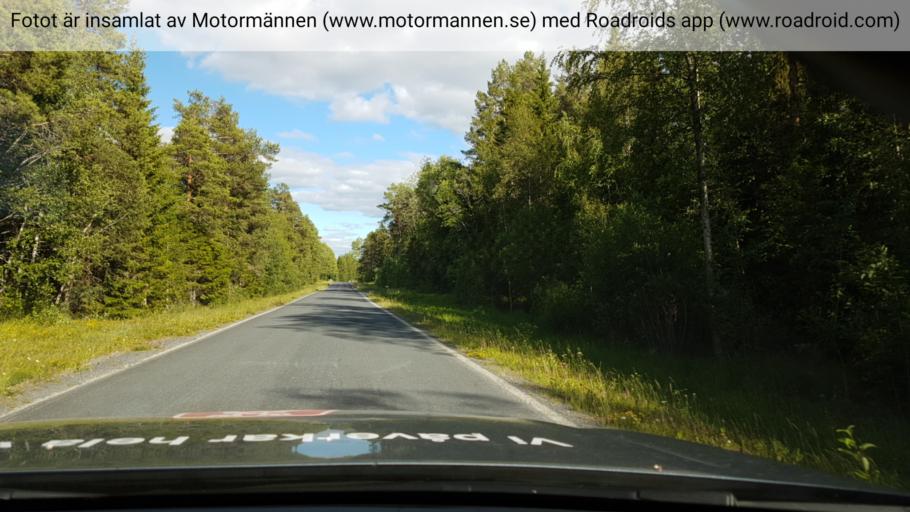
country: SE
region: Jaemtland
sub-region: Krokoms Kommun
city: Valla
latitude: 63.2863
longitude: 13.8812
